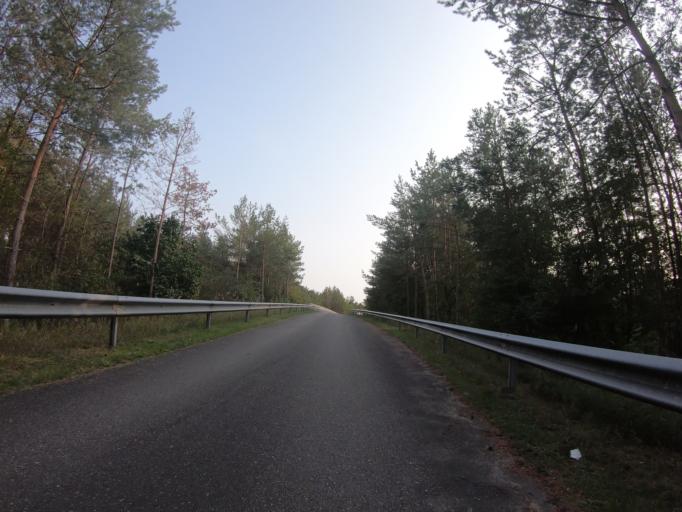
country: DE
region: Lower Saxony
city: Leiferde
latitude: 52.4571
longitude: 10.4494
